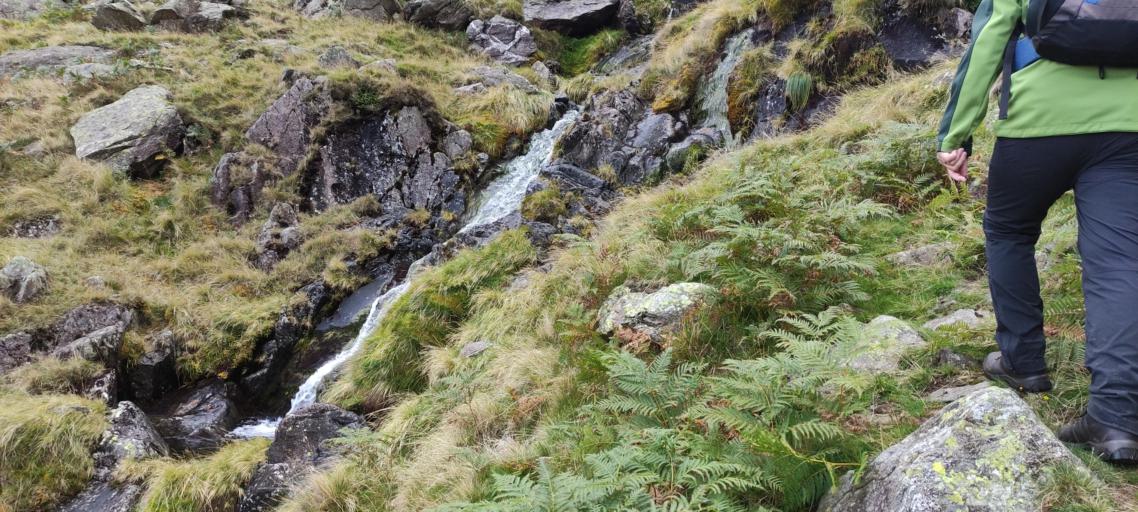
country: GB
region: England
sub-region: Cumbria
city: Ambleside
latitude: 54.3927
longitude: -3.1021
